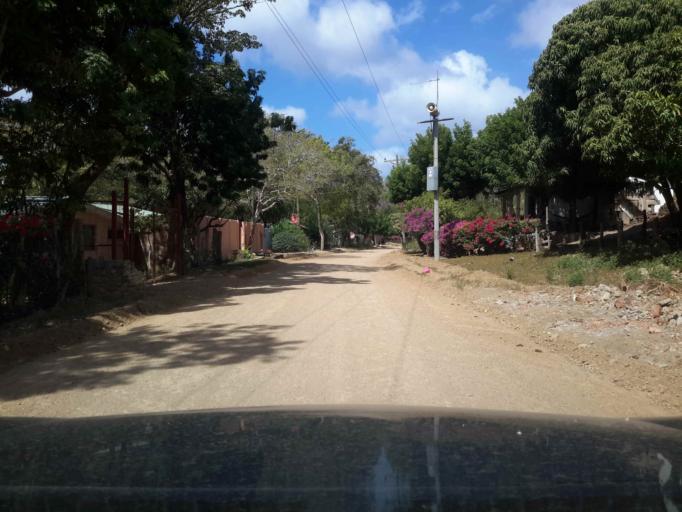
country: NI
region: Rivas
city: San Juan del Sur
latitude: 11.1565
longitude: -85.8005
